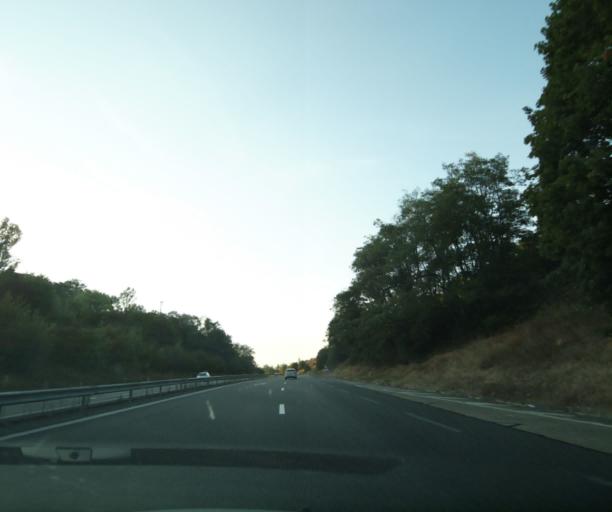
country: FR
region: Aquitaine
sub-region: Departement du Lot-et-Garonne
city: Boe
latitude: 44.1425
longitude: 0.6348
